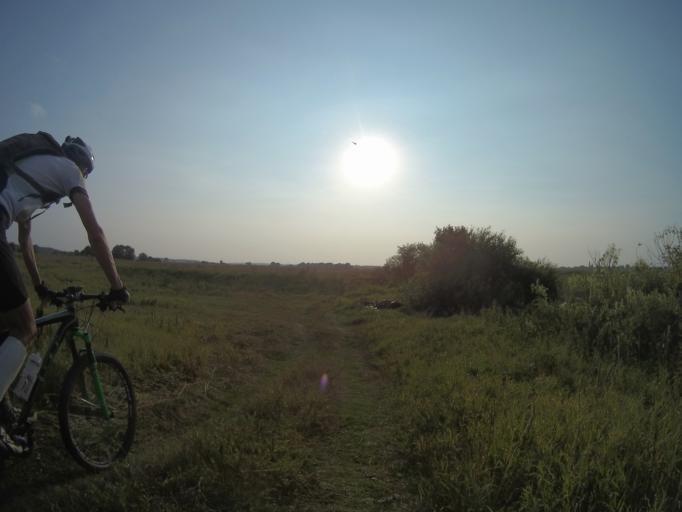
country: RU
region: Vladimir
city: Orgtrud
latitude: 56.3098
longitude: 40.6582
